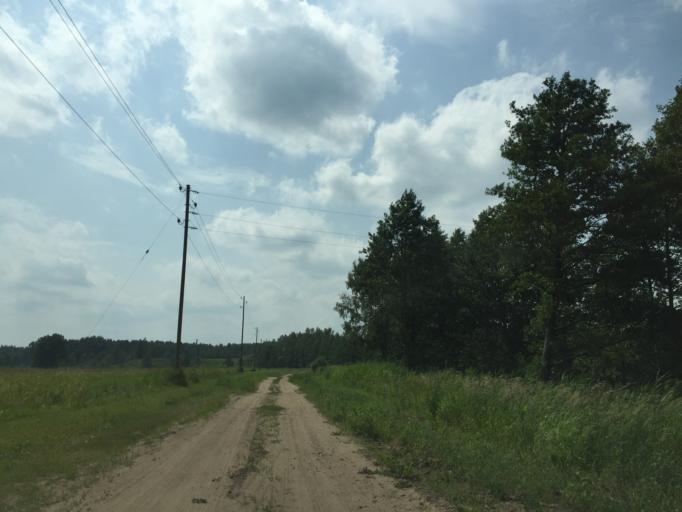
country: LV
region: Olaine
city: Olaine
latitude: 56.7754
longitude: 23.9177
